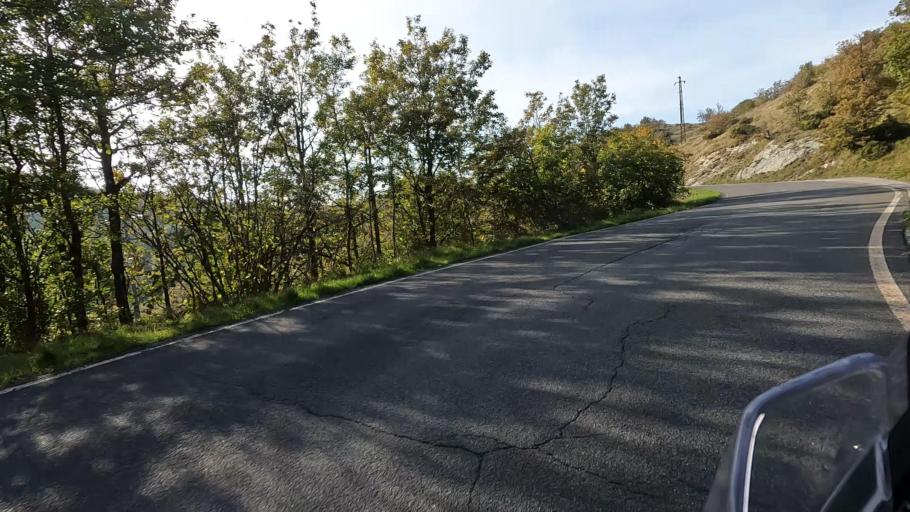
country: IT
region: Liguria
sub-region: Provincia di Savona
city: Urbe
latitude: 44.4763
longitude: 8.5684
